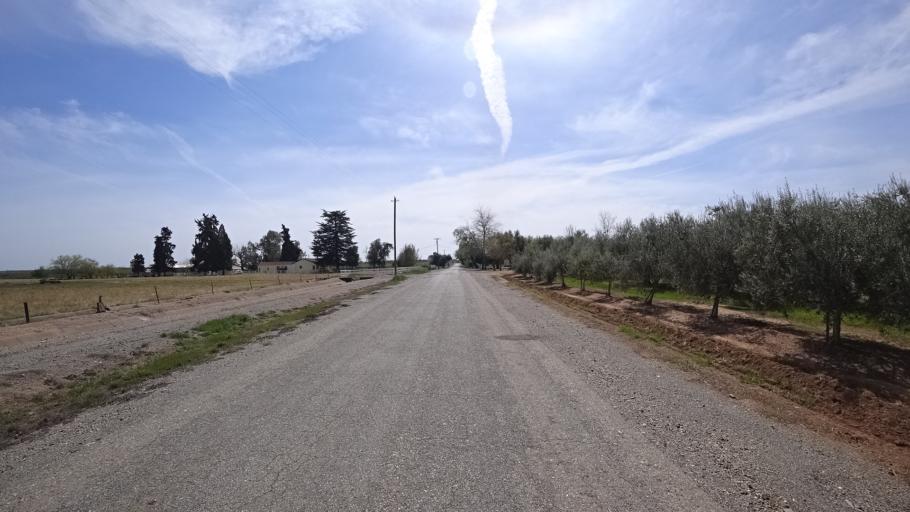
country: US
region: California
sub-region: Glenn County
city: Orland
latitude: 39.7924
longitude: -122.1504
